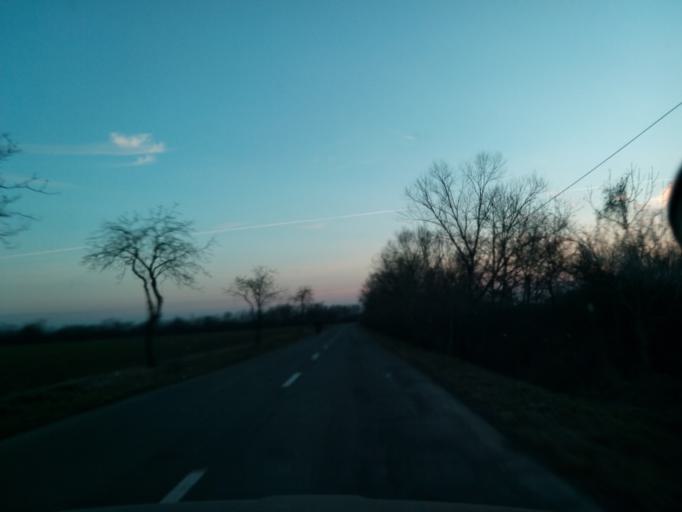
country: SK
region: Kosicky
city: Sobrance
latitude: 48.7969
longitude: 22.1475
